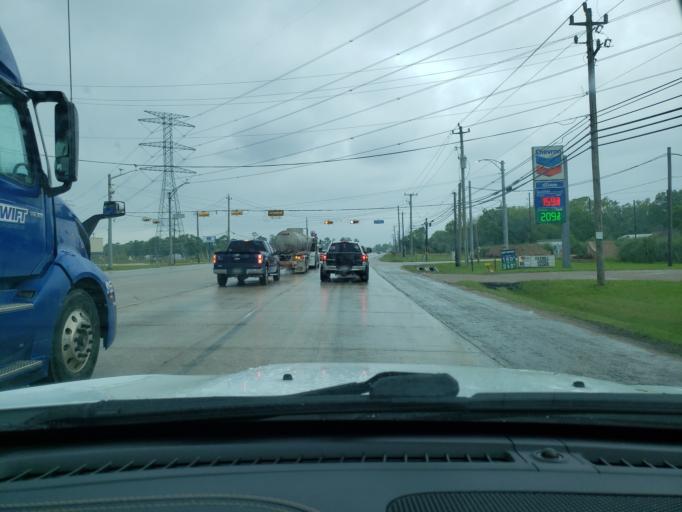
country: US
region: Texas
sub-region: Chambers County
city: Mont Belvieu
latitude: 29.7984
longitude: -94.9058
